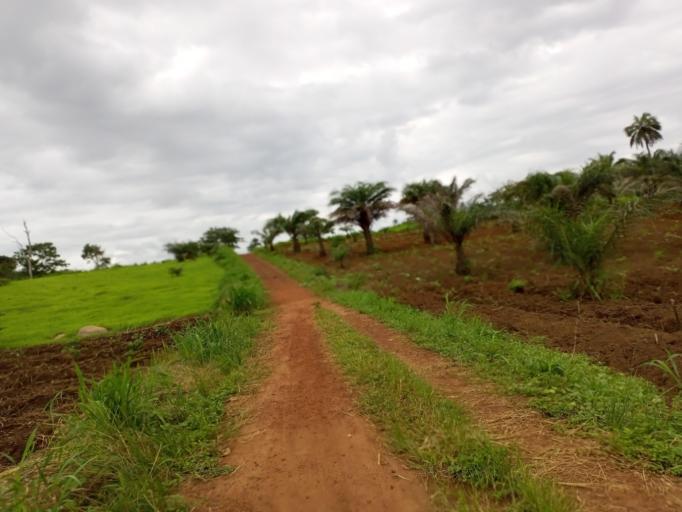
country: SL
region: Northern Province
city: Kamakwie
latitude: 9.5050
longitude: -12.2674
